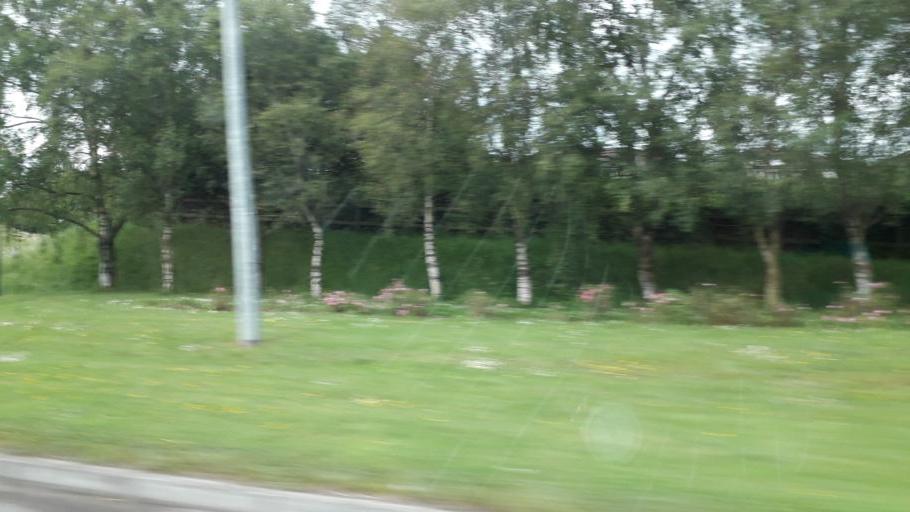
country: IE
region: Leinster
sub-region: County Carlow
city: Bagenalstown
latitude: 52.7345
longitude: -6.9868
